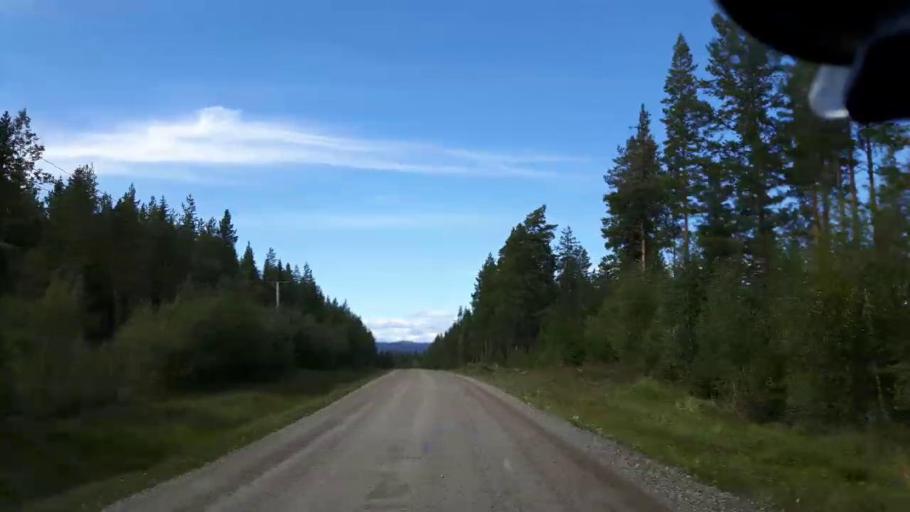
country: SE
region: Jaemtland
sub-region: Ragunda Kommun
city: Hammarstrand
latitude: 63.1423
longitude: 16.2259
